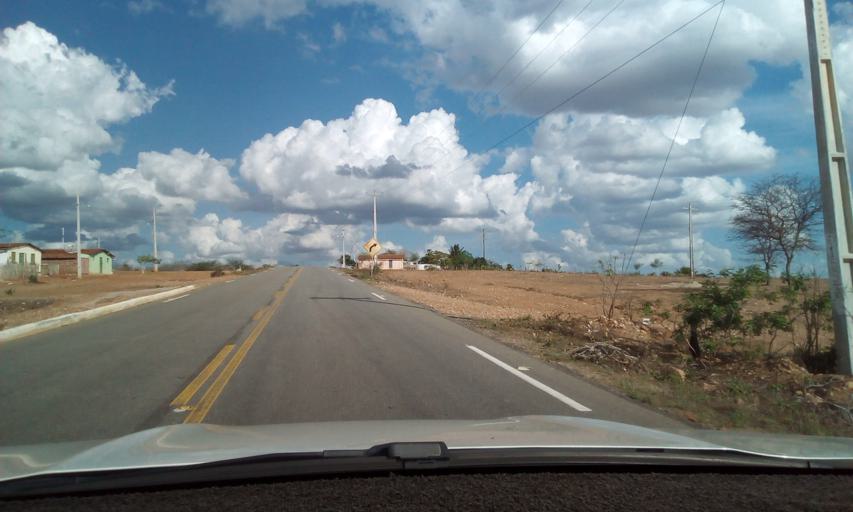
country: BR
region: Paraiba
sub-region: Soledade
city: Soledade
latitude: -6.7960
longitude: -36.4083
